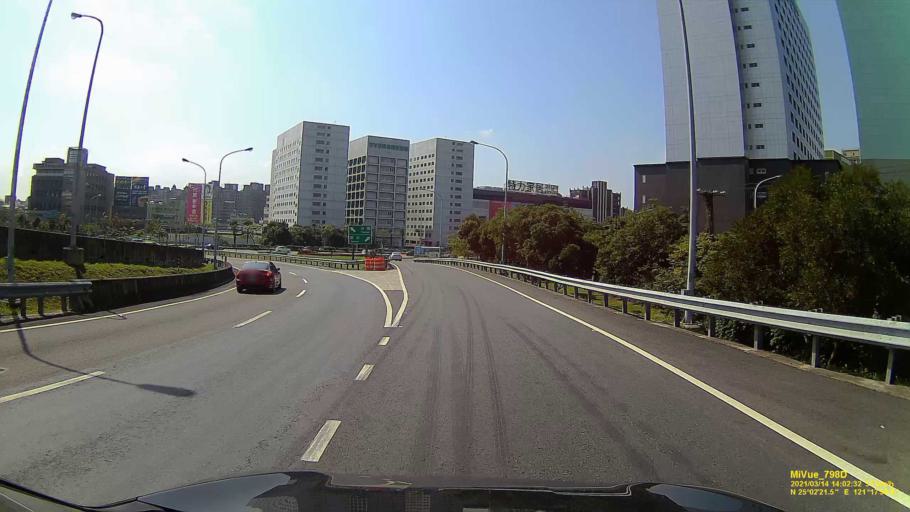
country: TW
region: Taiwan
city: Taoyuan City
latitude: 25.0399
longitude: 121.2982
